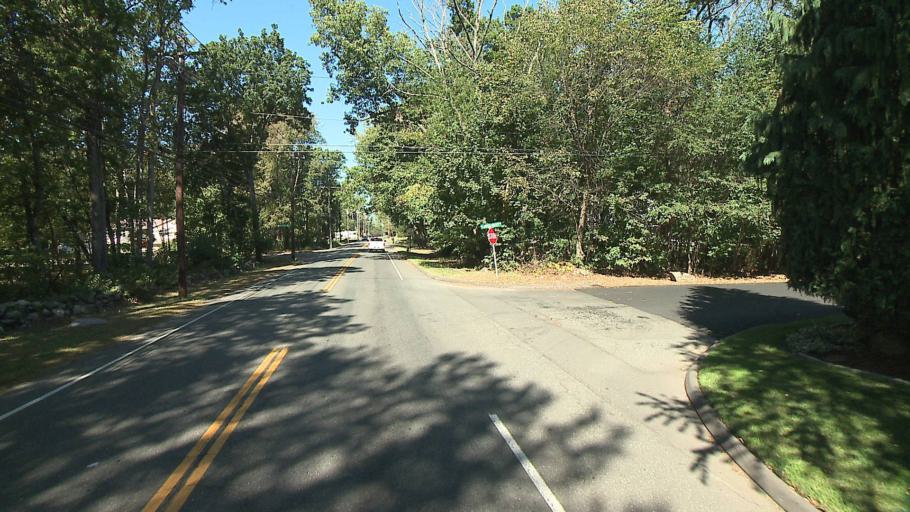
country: US
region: Connecticut
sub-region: New Haven County
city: Orange
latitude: 41.3023
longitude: -73.0437
